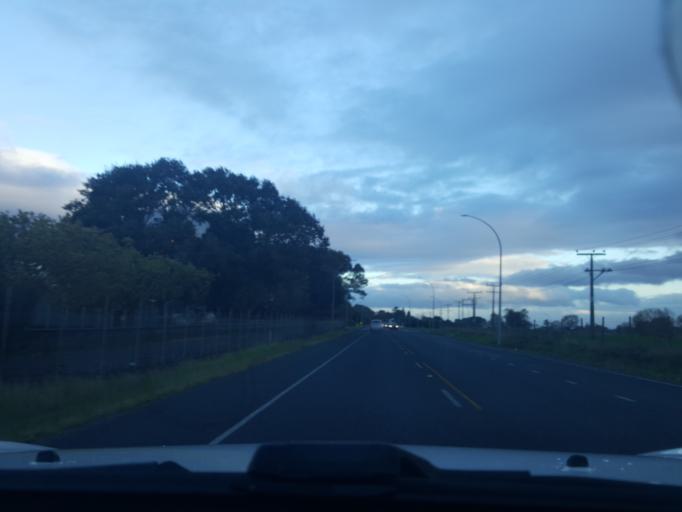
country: NZ
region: Waikato
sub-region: Waikato District
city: Ngaruawahia
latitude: -37.7165
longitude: 175.2124
